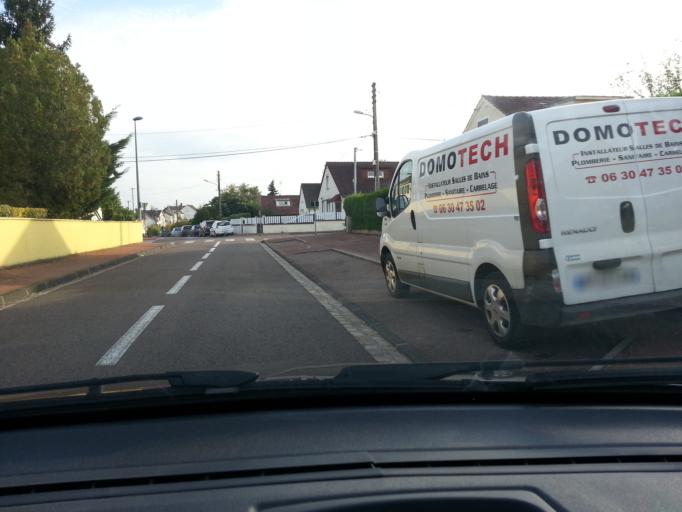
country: FR
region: Bourgogne
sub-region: Departement de Saone-et-Loire
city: Chatenoy-le-Royal
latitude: 46.7817
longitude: 4.8240
